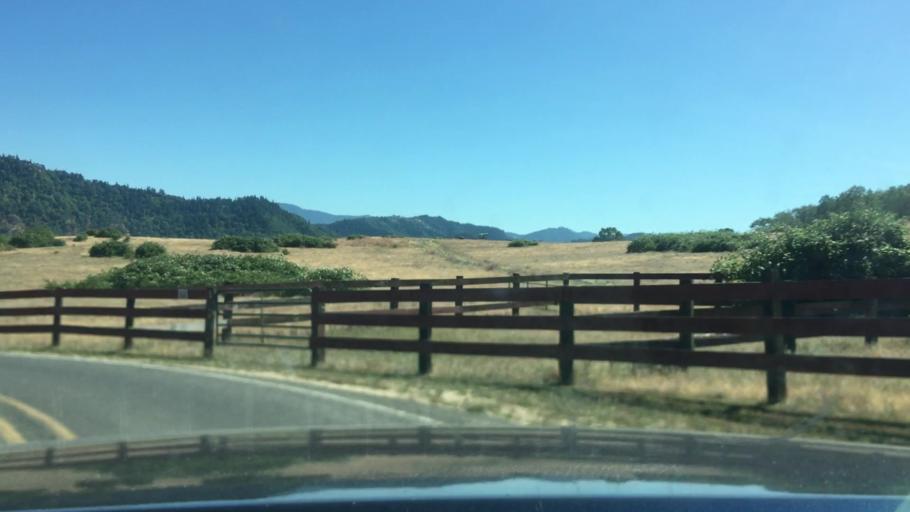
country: US
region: Oregon
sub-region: Douglas County
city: Winston
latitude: 43.1307
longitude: -123.4146
